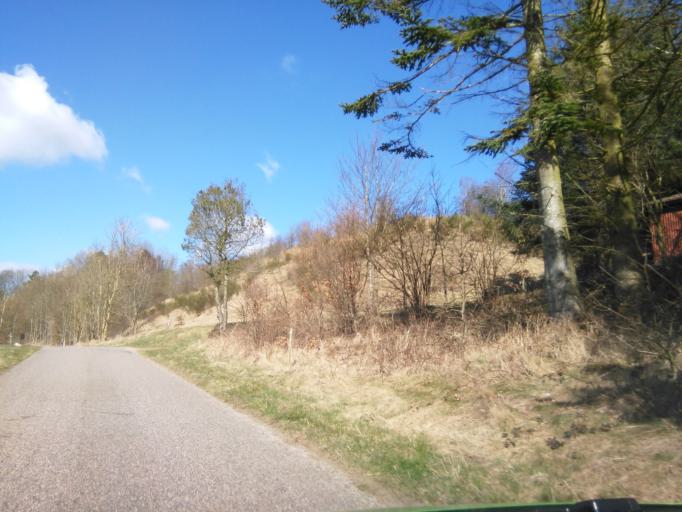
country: DK
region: Central Jutland
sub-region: Skanderborg Kommune
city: Ry
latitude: 56.1100
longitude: 9.7372
